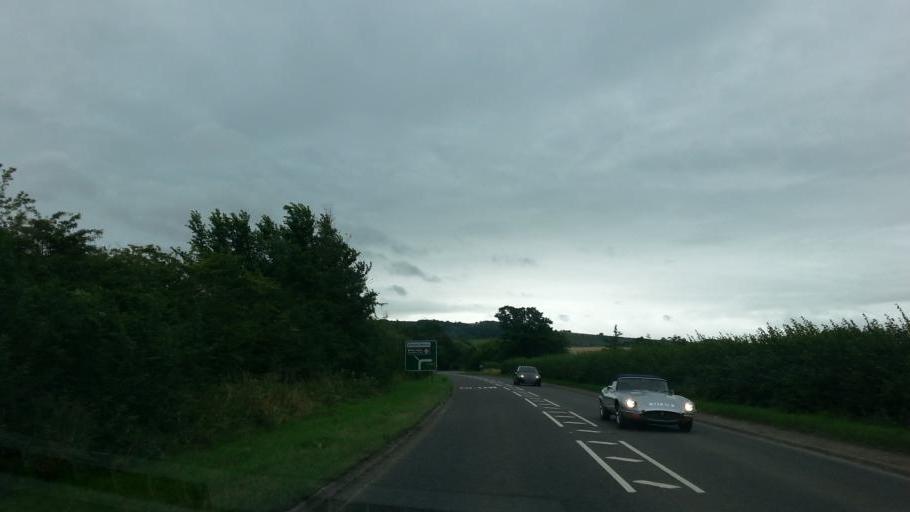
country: GB
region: England
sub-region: Wiltshire
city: Westbury
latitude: 51.2741
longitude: -2.1789
